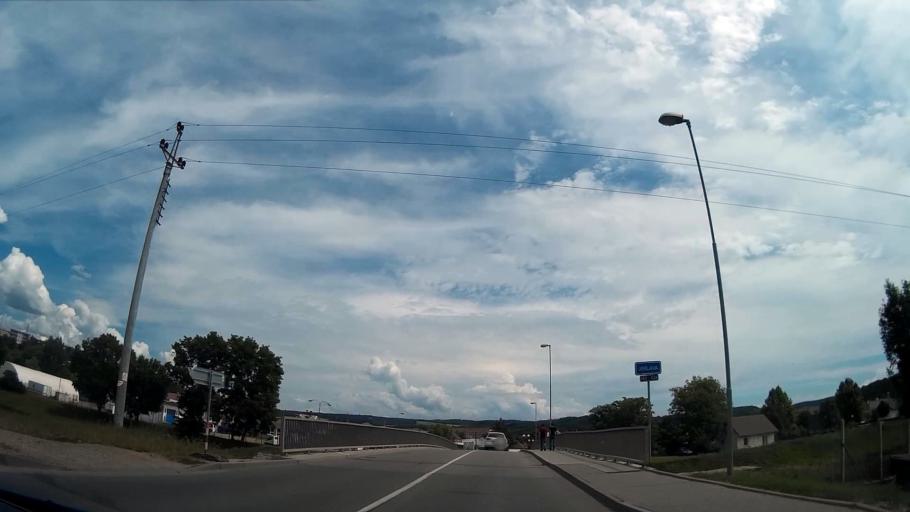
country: CZ
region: South Moravian
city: Ivancice
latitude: 49.0961
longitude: 16.3686
